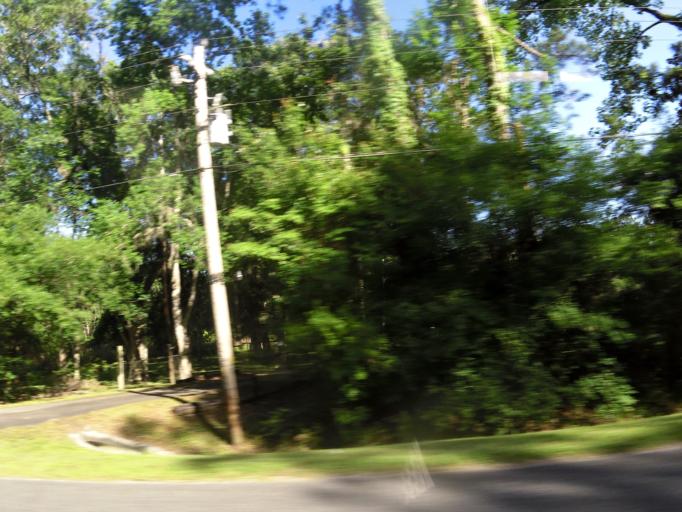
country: US
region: Florida
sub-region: Nassau County
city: Nassau Village-Ratliff
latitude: 30.4900
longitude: -81.8271
